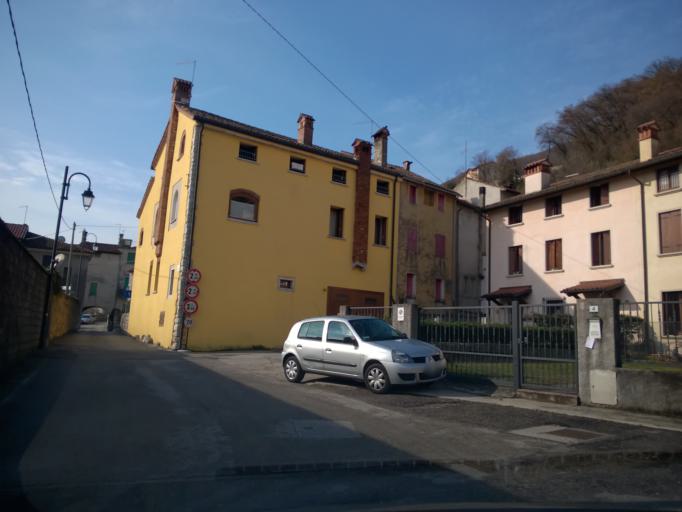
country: IT
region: Veneto
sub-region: Provincia di Vicenza
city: Piovene Rocchette
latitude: 45.7611
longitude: 11.4298
